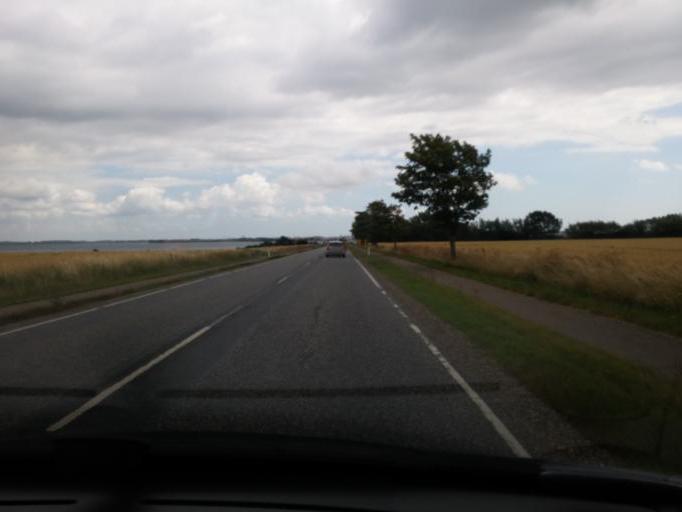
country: DK
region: South Denmark
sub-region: Langeland Kommune
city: Rudkobing
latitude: 54.9713
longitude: 10.6455
